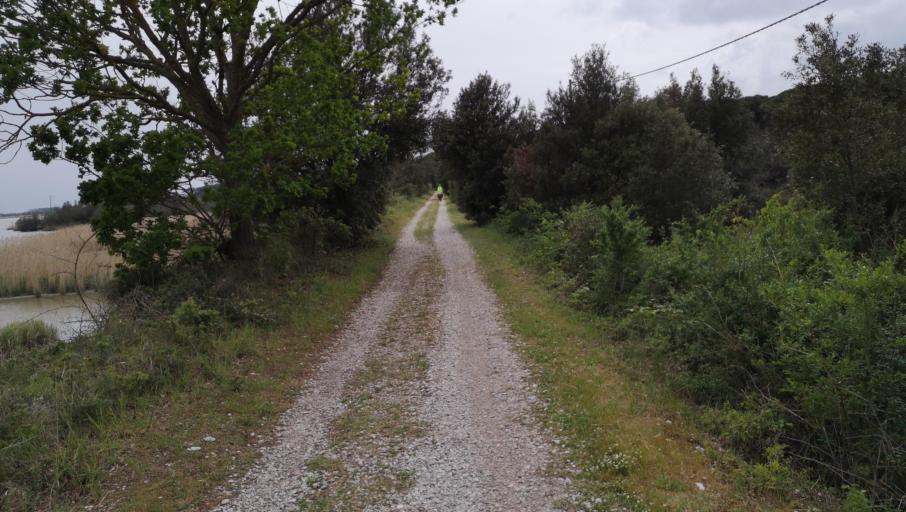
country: IT
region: Emilia-Romagna
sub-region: Provincia di Ferrara
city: Goro
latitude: 44.8264
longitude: 12.2673
